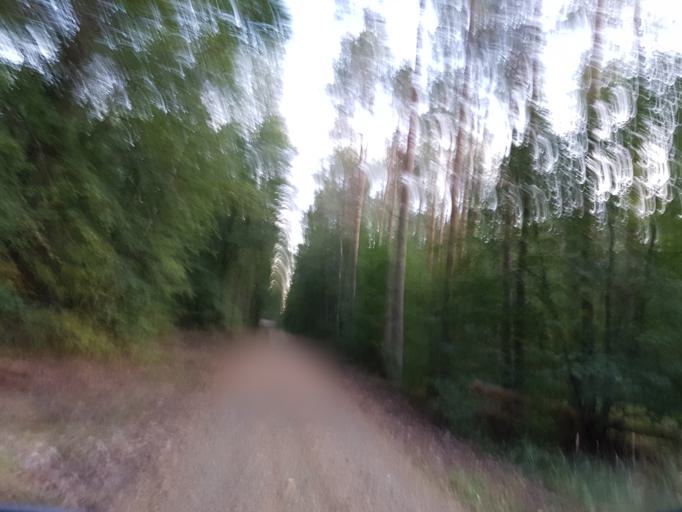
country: DE
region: Brandenburg
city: Trobitz
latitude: 51.5675
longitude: 13.4459
